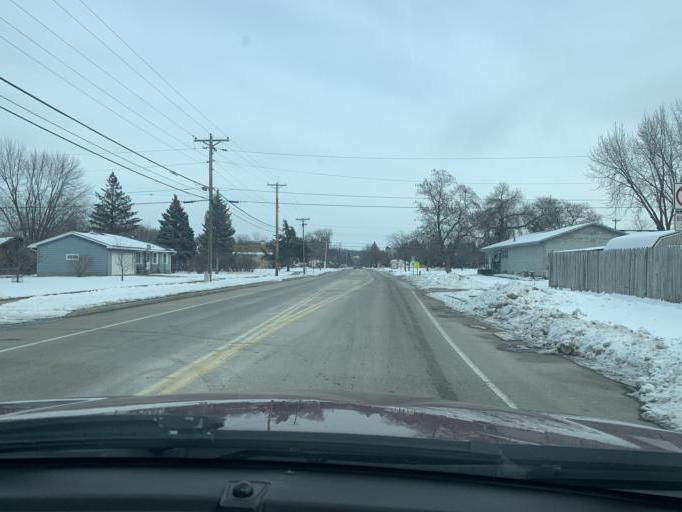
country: US
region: Minnesota
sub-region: Washington County
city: Saint Paul Park
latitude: 44.8366
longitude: -92.9838
